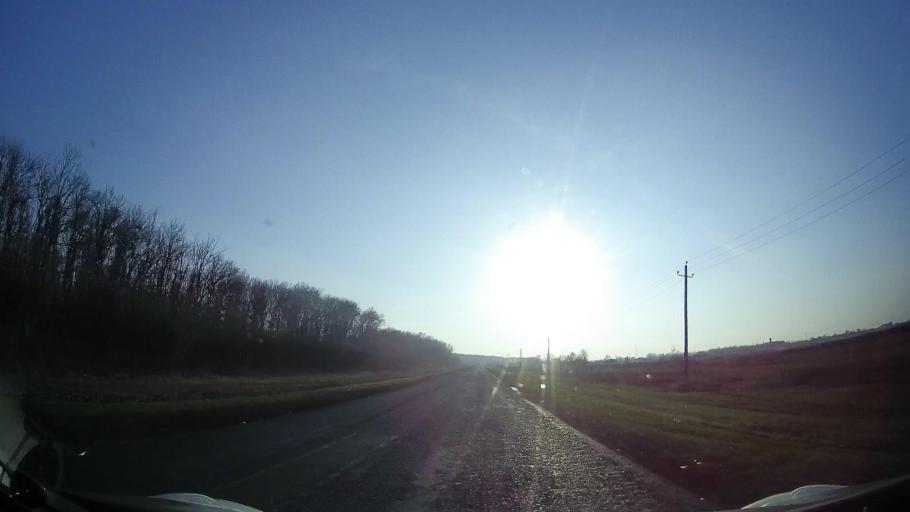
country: RU
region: Rostov
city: Ol'ginskaya
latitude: 47.1416
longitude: 39.9006
